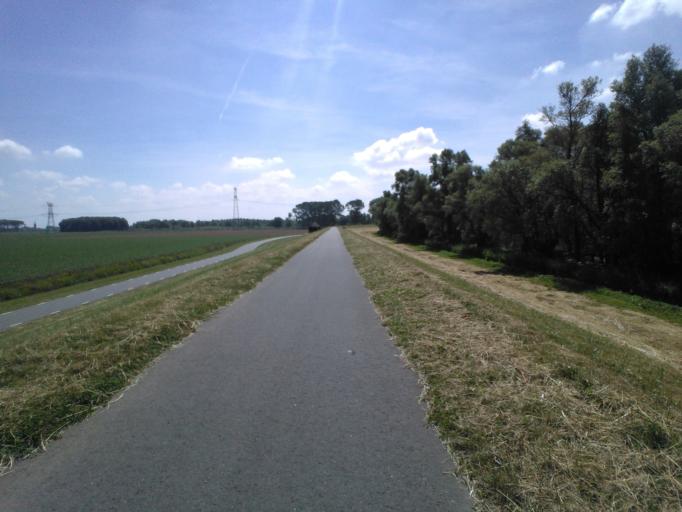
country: NL
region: North Brabant
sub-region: Gemeente Geertruidenberg
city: Geertruidenberg
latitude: 51.7351
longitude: 4.8553
